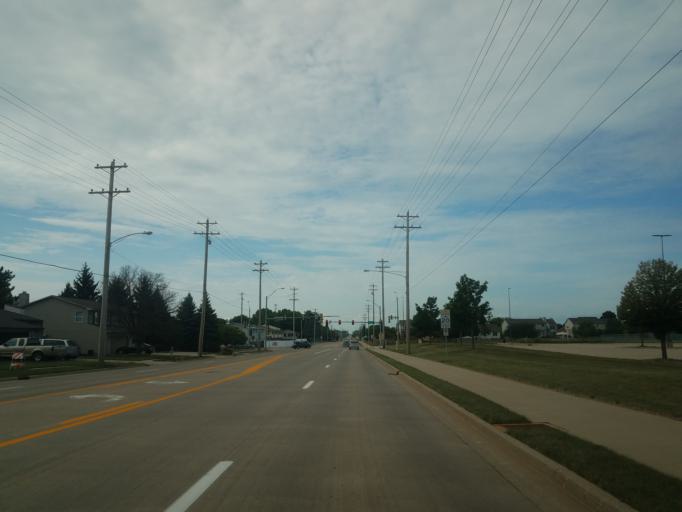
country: US
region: Illinois
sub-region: McLean County
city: Normal
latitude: 40.4946
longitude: -88.9239
